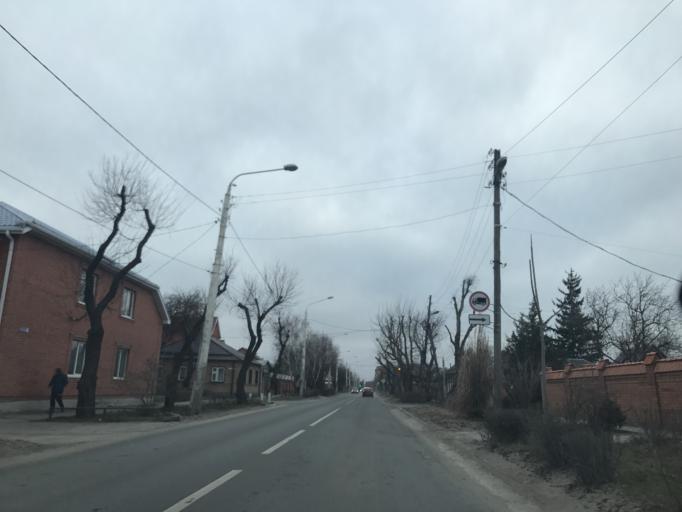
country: RU
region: Rostov
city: Rostov-na-Donu
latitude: 47.2072
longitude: 39.6644
